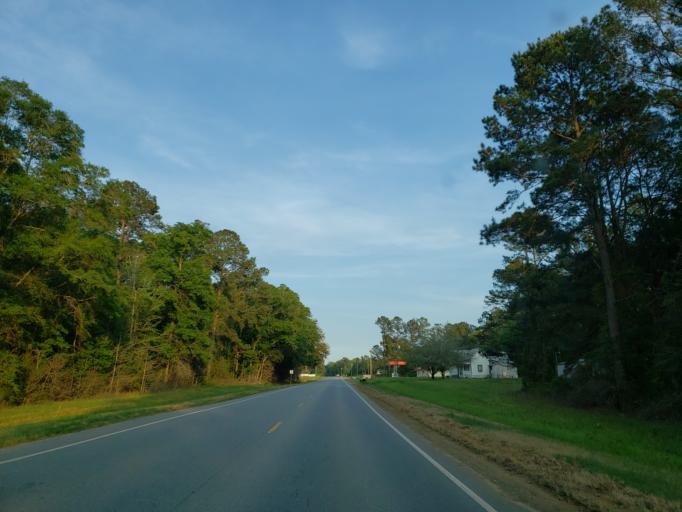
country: US
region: Georgia
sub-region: Lowndes County
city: Hahira
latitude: 30.9970
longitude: -83.4405
